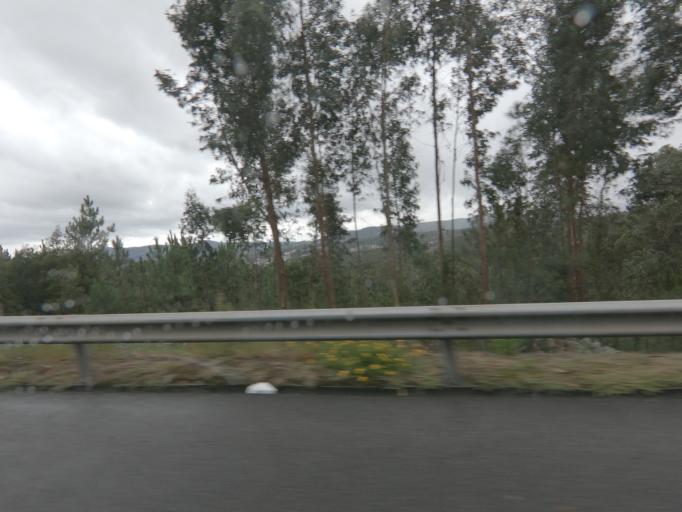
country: PT
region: Porto
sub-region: Paredes
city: Recarei
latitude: 41.1686
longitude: -8.4066
